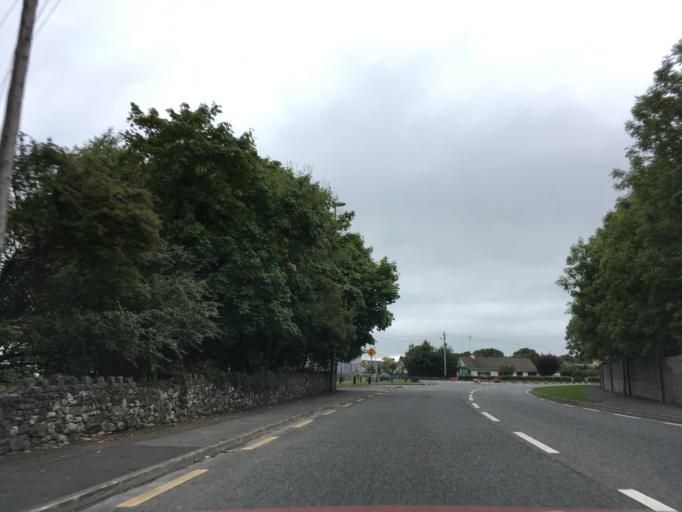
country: IE
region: Munster
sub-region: An Clar
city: Ennis
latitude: 52.8307
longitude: -8.9911
